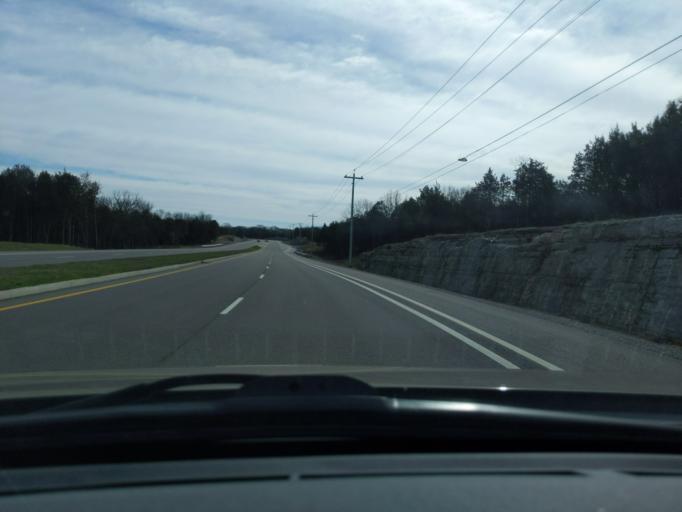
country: US
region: Tennessee
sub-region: Wilson County
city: Mount Juliet
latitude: 36.1920
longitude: -86.4777
